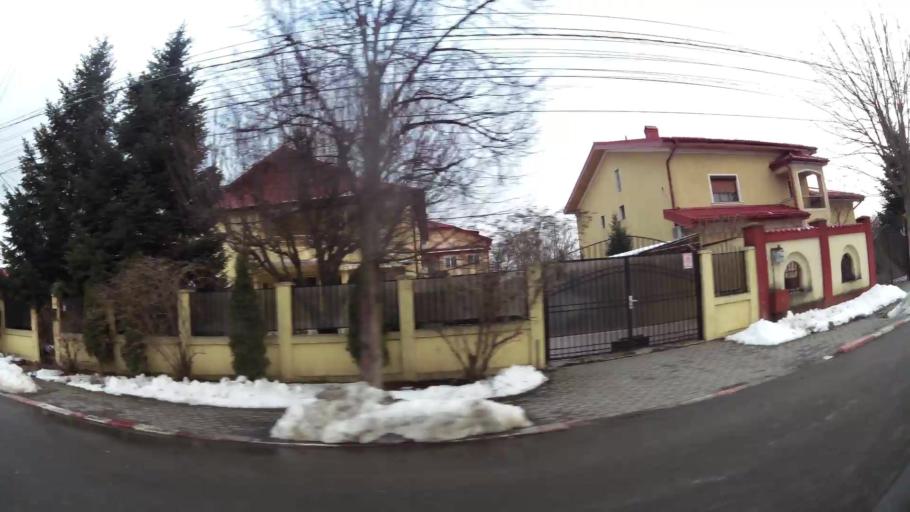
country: RO
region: Ilfov
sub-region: Voluntari City
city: Voluntari
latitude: 44.4971
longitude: 26.1685
